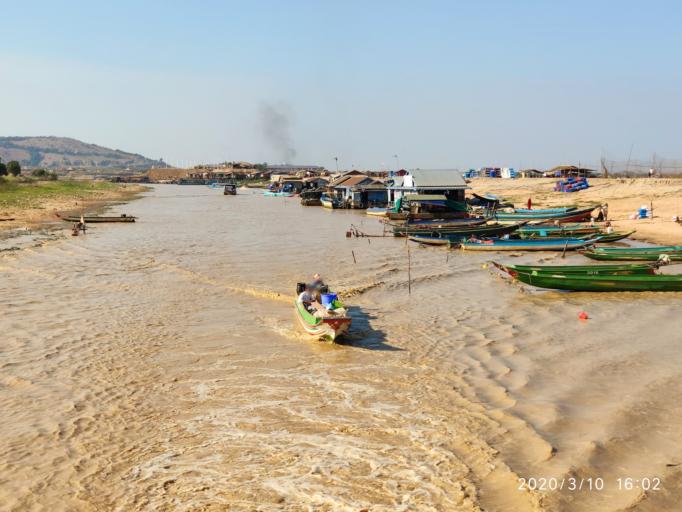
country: KH
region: Siem Reap
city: Siem Reap
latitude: 13.2585
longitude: 103.8232
